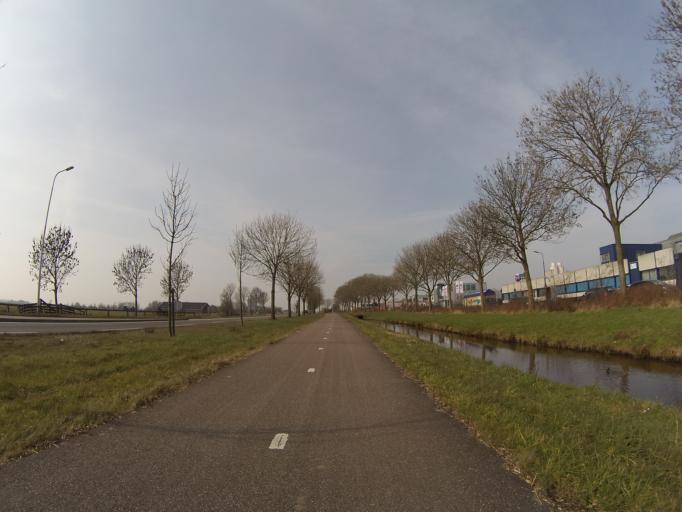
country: NL
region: Utrecht
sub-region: Gemeente Bunschoten
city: Bunschoten
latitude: 52.2280
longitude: 5.3623
